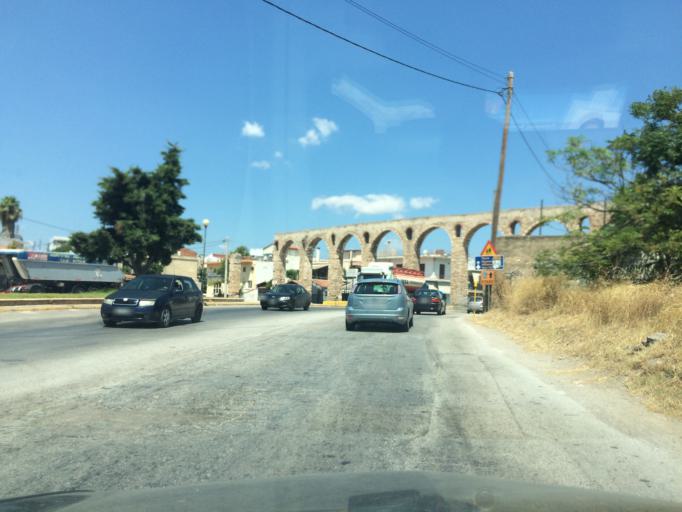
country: GR
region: Central Greece
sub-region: Nomos Evvoias
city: Chalkida
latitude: 38.4607
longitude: 23.6115
